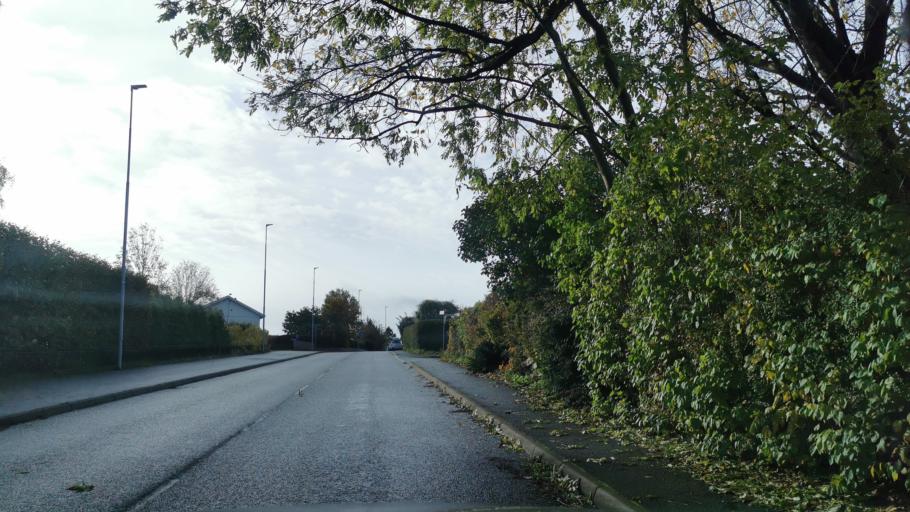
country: SE
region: Vaestra Goetaland
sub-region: Partille Kommun
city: Partille
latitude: 57.7308
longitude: 12.0818
